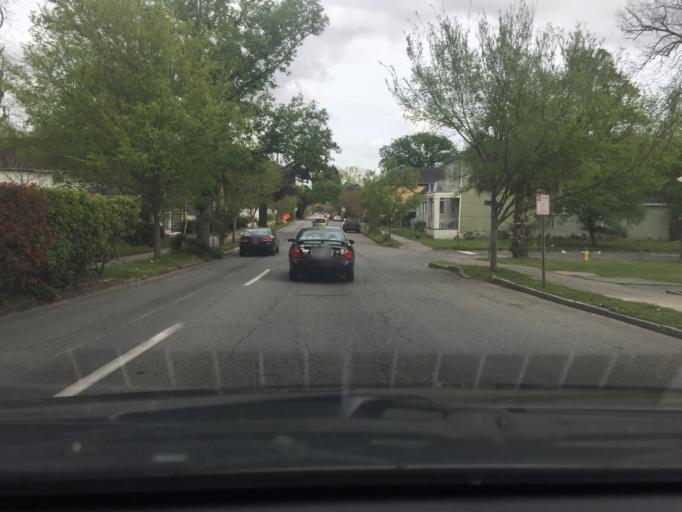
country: US
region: Georgia
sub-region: Chatham County
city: Savannah
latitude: 32.0603
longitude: -81.0901
